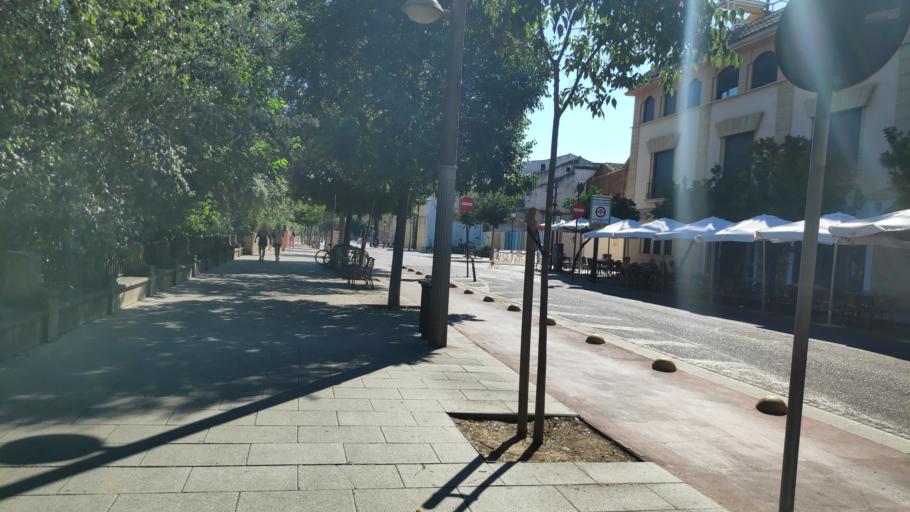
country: ES
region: Andalusia
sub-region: Province of Cordoba
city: Cordoba
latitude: 37.8785
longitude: -4.7776
